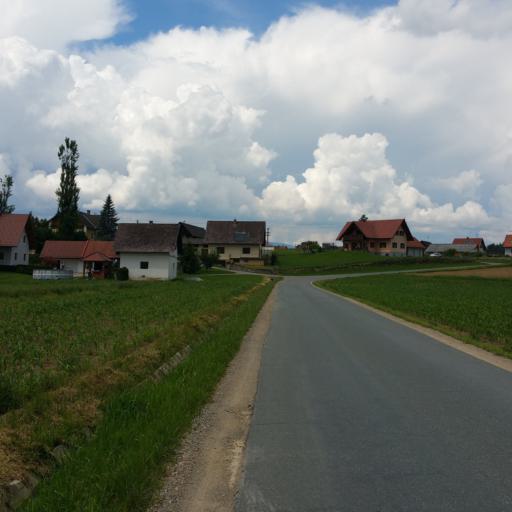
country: AT
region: Styria
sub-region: Politischer Bezirk Leibnitz
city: Gleinstatten
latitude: 46.7445
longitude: 15.3533
